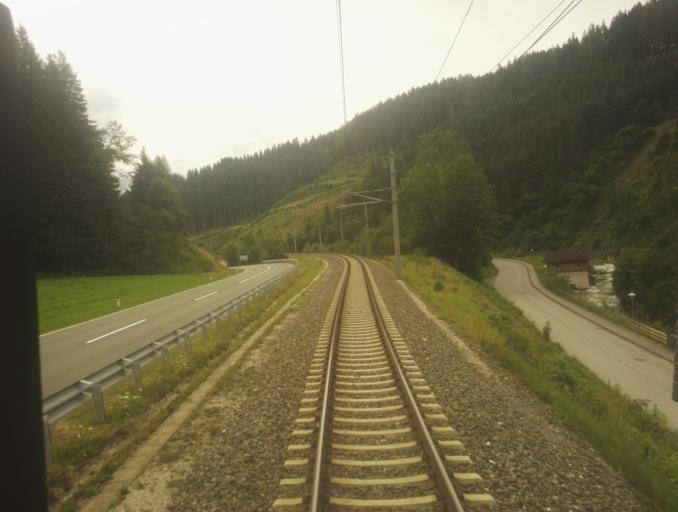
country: AT
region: Salzburg
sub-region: Politischer Bezirk Sankt Johann im Pongau
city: Huttau
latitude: 47.4221
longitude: 13.3395
